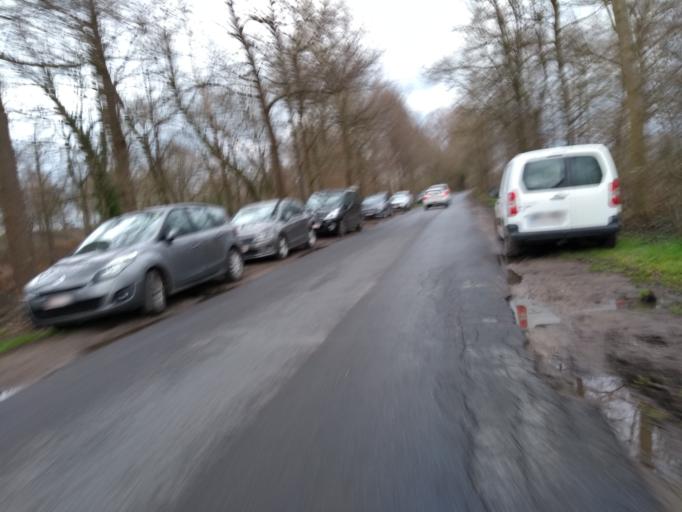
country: BE
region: Flanders
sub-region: Provincie Oost-Vlaanderen
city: Aalter
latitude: 51.1011
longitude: 3.4199
